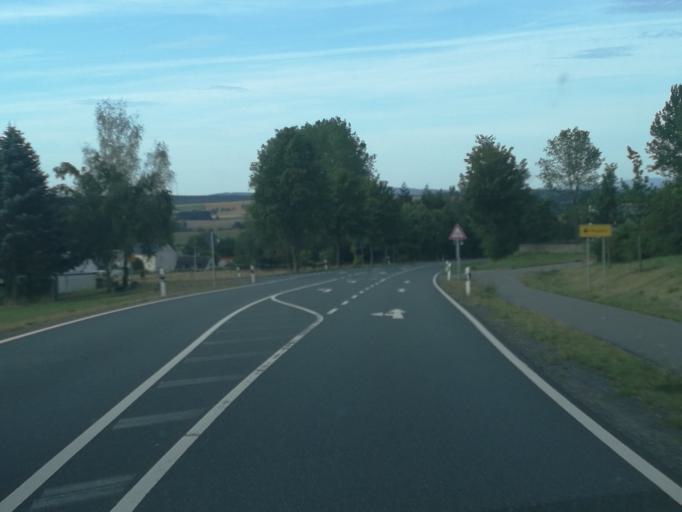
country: DE
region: Bavaria
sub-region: Upper Franconia
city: Regnitzlosau
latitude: 50.3374
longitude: 12.0730
